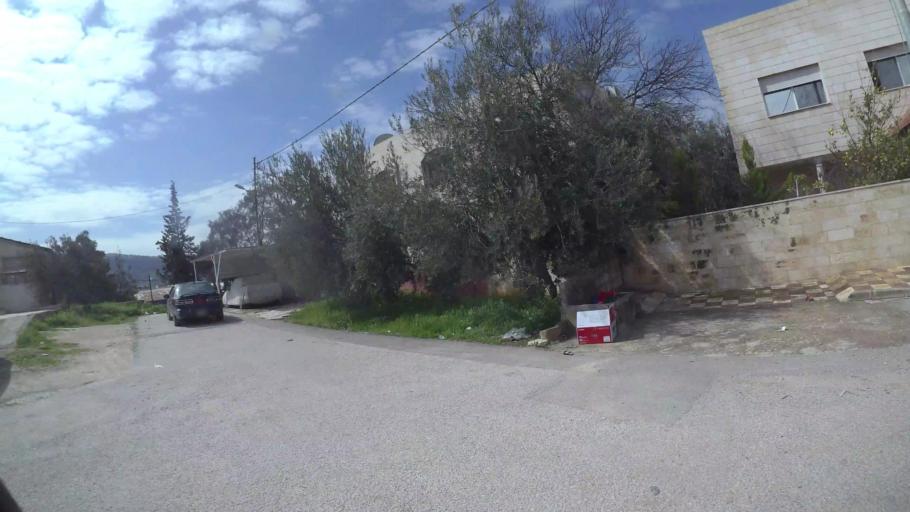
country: JO
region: Amman
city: Al Jubayhah
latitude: 32.0613
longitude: 35.8240
